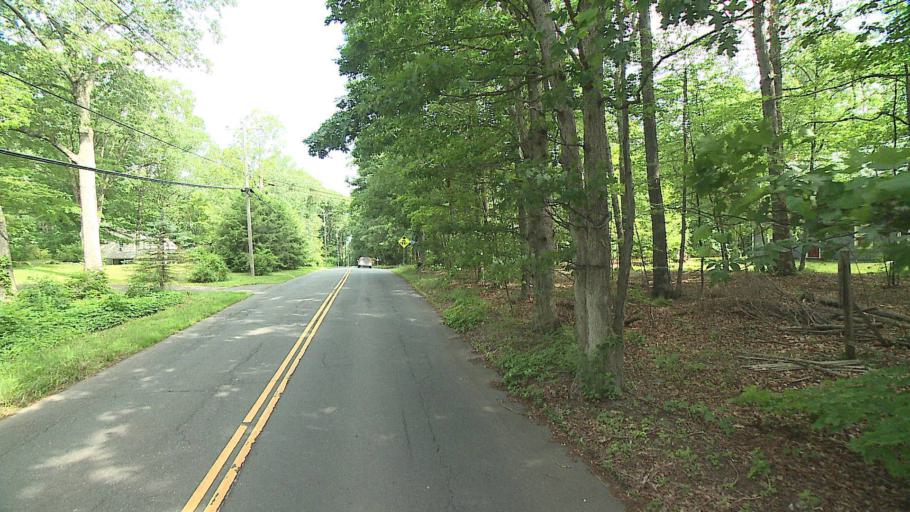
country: US
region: Connecticut
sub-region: New Haven County
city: Southbury
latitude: 41.4623
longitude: -73.1997
